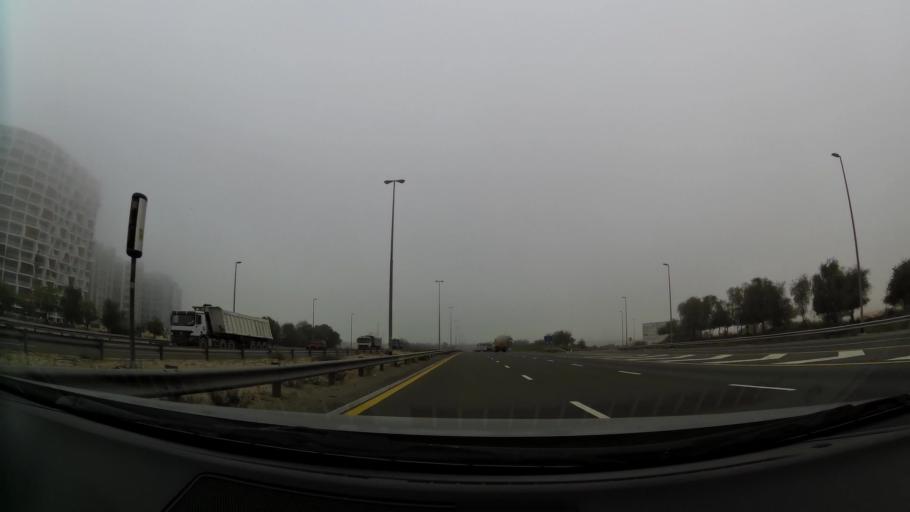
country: AE
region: Dubai
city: Dubai
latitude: 25.1078
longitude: 55.3752
